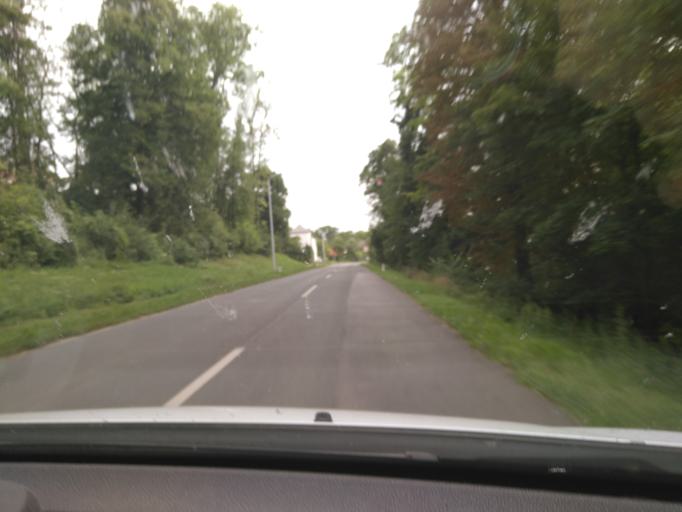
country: AT
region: Burgenland
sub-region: Politischer Bezirk Oberpullendorf
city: Nikitsch
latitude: 47.5314
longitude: 16.6490
